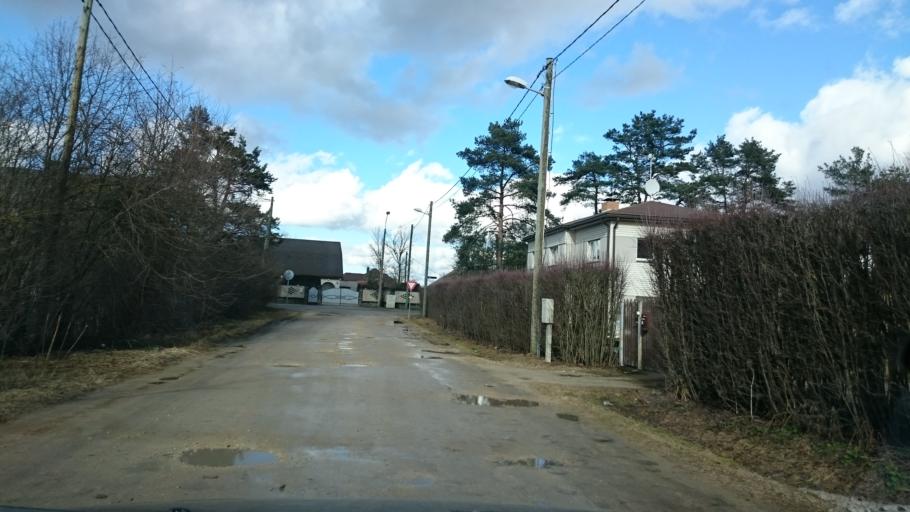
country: LV
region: Stopini
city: Ulbroka
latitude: 56.9565
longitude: 24.2882
